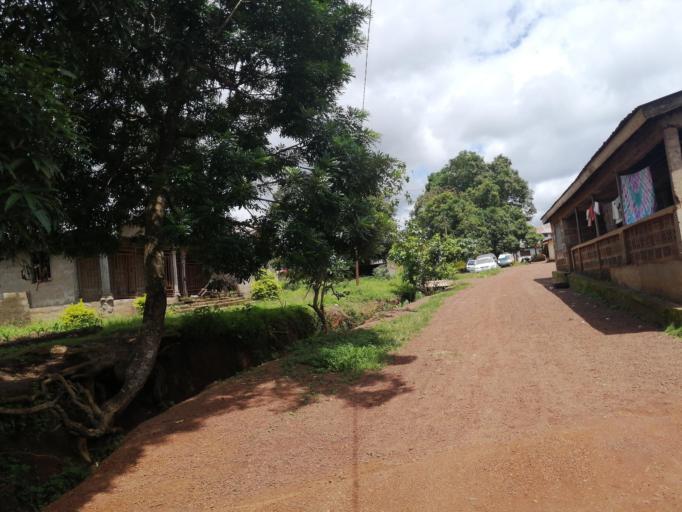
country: SL
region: Northern Province
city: Port Loko
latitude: 8.7694
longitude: -12.7824
